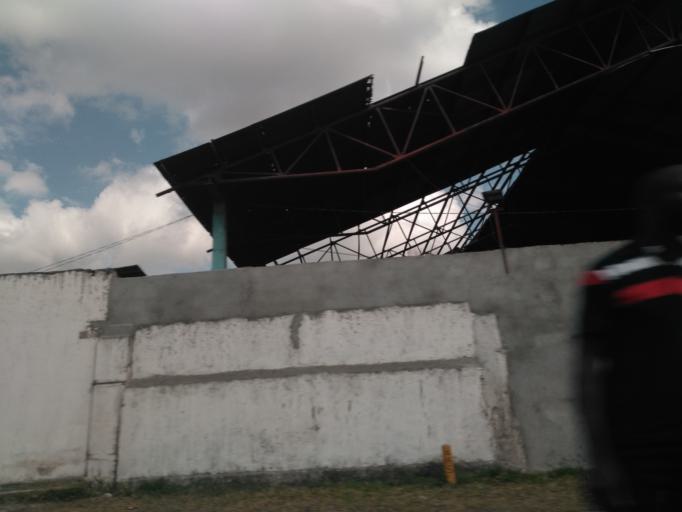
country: TZ
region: Dar es Salaam
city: Magomeni
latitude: -6.7622
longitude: 39.2373
